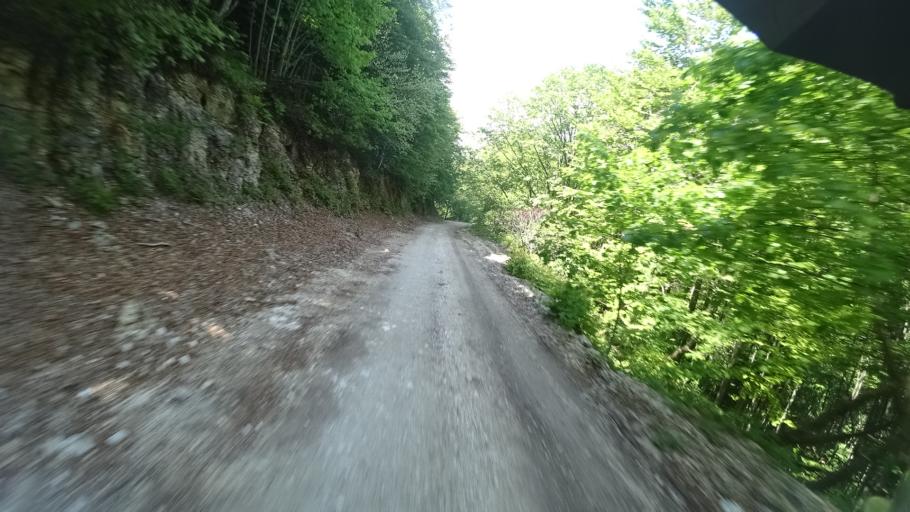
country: BA
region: Federation of Bosnia and Herzegovina
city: Orasac
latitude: 44.5751
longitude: 15.8587
